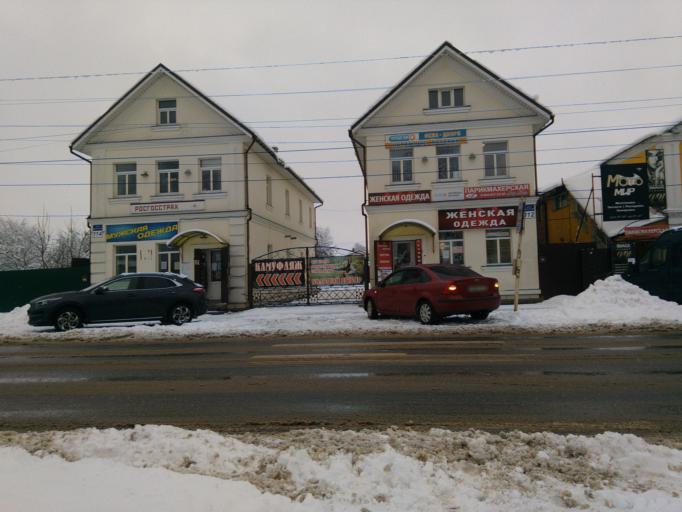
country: RU
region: Tverskaya
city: Torzhok
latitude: 57.0444
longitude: 34.9689
